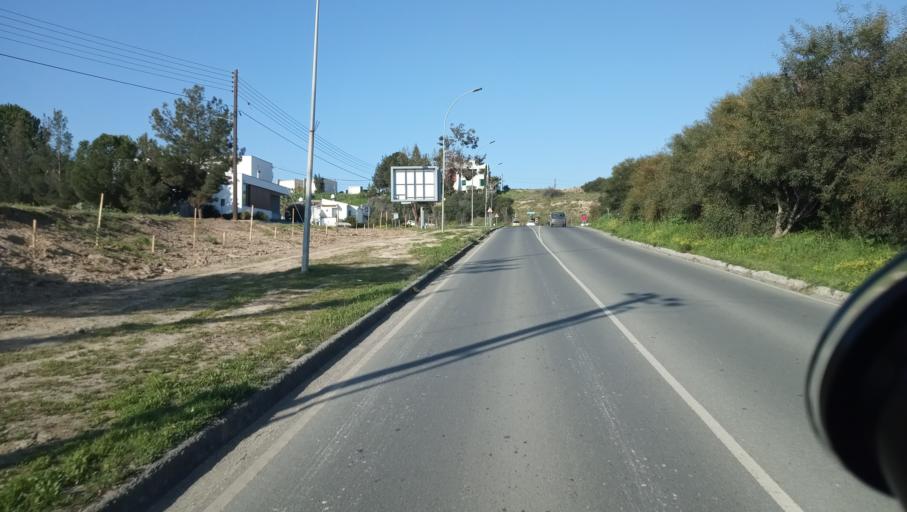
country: CY
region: Lefkosia
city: Nicosia
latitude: 35.1486
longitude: 33.3098
